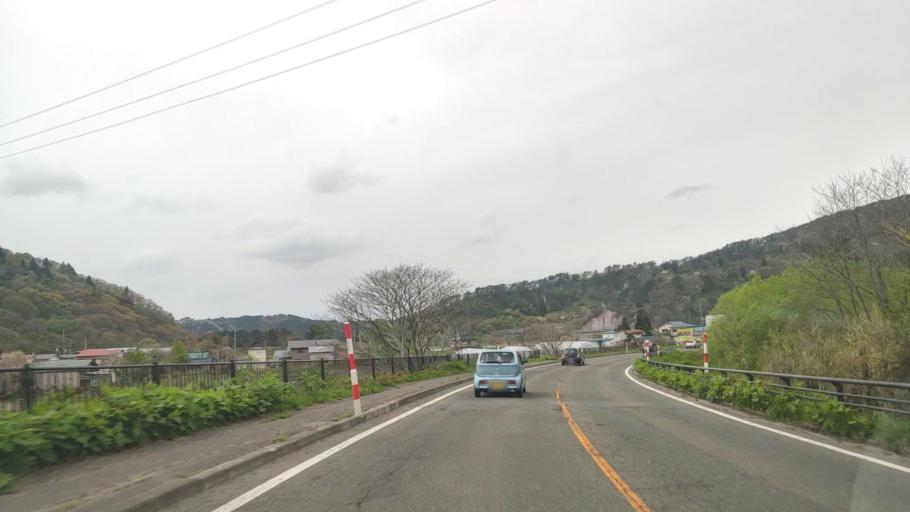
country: JP
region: Akita
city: Takanosu
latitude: 40.2120
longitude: 140.2625
